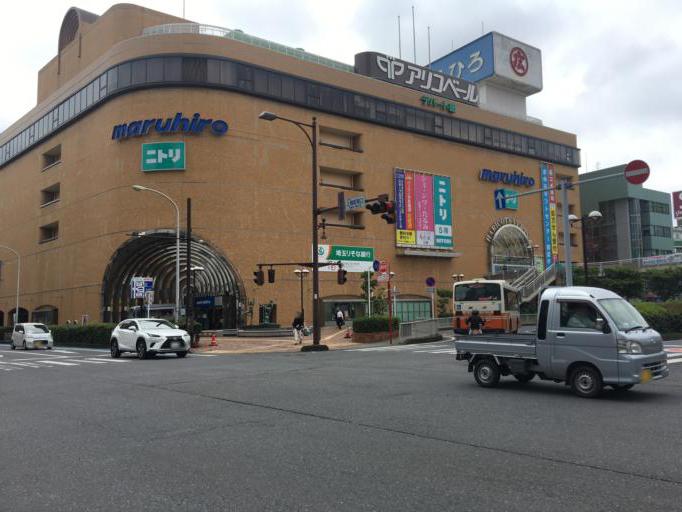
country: JP
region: Saitama
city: Ageoshimo
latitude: 35.9741
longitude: 139.5895
